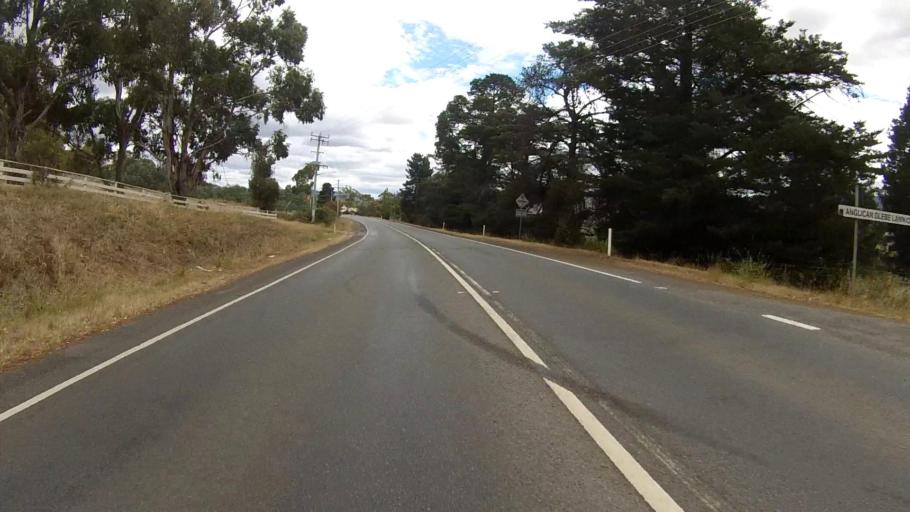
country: AU
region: Tasmania
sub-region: Brighton
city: Bridgewater
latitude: -42.6798
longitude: 147.2657
